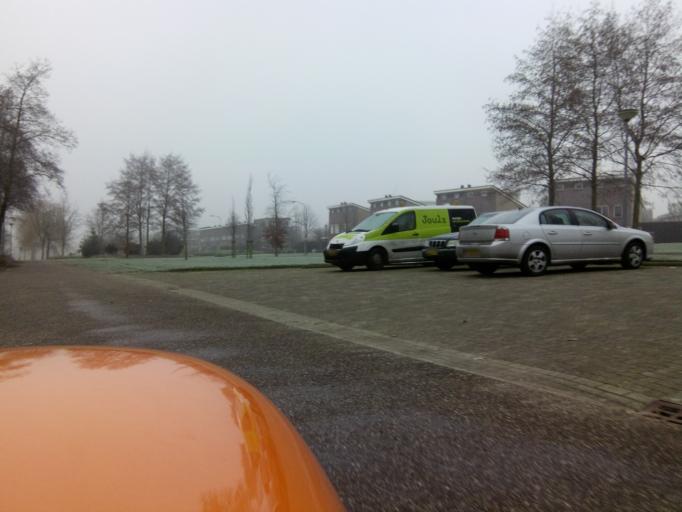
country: NL
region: Gelderland
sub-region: Gemeente Barneveld
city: Zwartebroek
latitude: 52.1698
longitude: 5.4689
